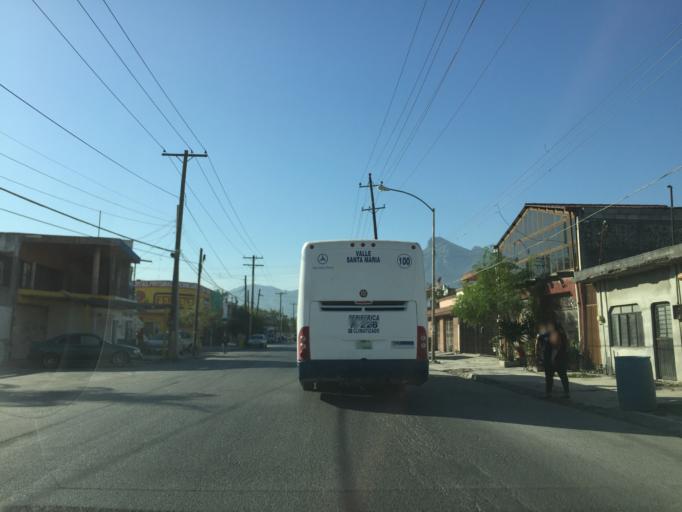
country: MX
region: Nuevo Leon
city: Guadalupe
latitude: 25.6990
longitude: -100.2170
